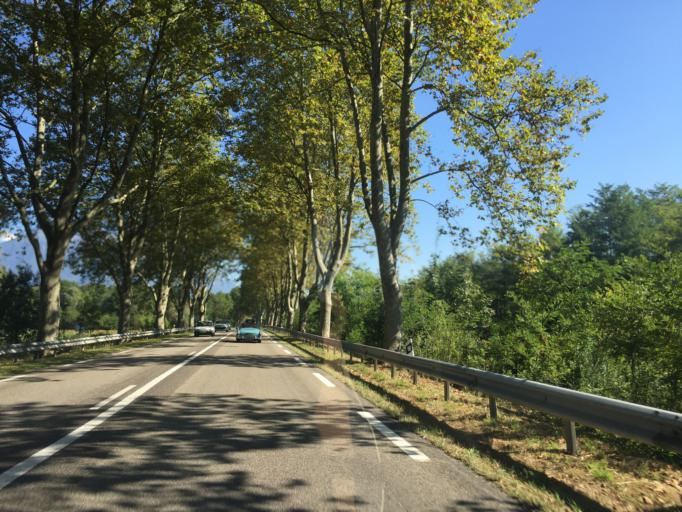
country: FR
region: Rhone-Alpes
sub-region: Departement de la Savoie
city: Cruet
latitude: 45.5203
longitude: 6.1023
